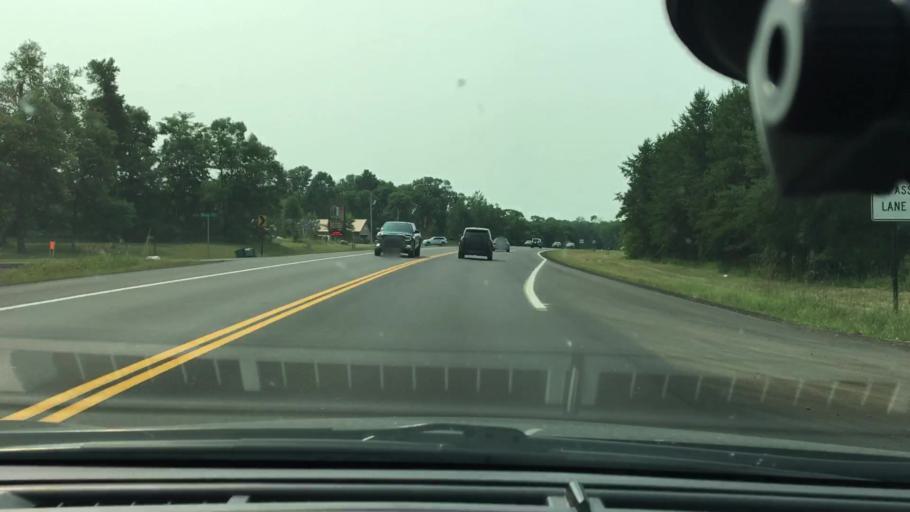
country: US
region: Minnesota
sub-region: Crow Wing County
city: Brainerd
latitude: 46.4380
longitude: -94.1715
